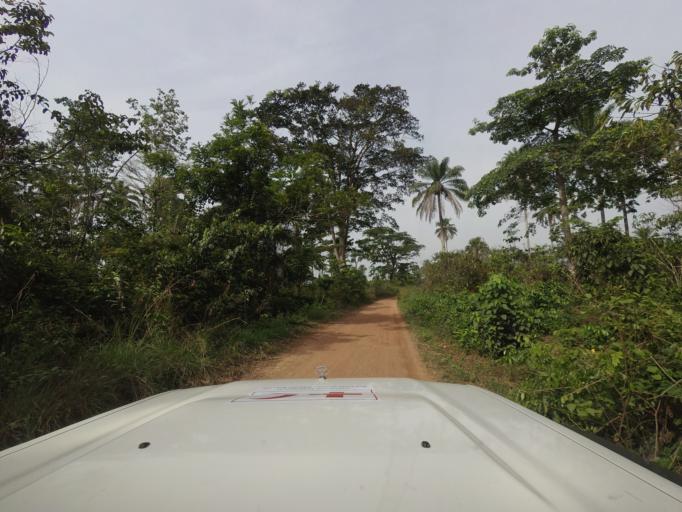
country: GN
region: Nzerekore
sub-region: Macenta
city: Macenta
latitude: 8.5212
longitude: -9.5135
